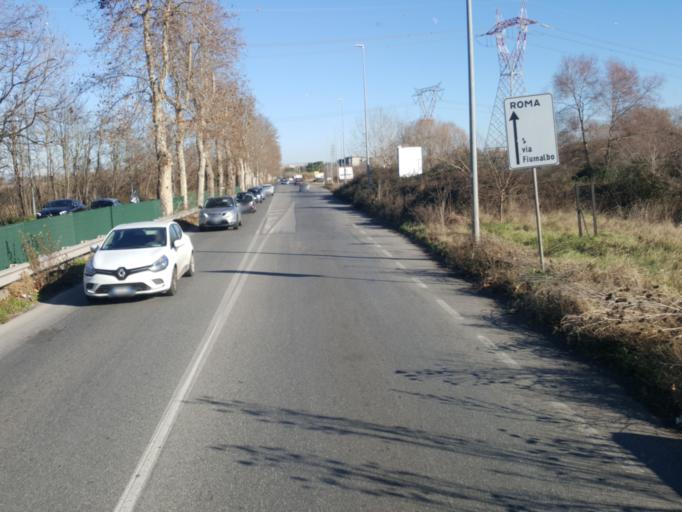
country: IT
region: Latium
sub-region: Citta metropolitana di Roma Capitale
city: Vitinia
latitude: 41.7929
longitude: 12.3907
